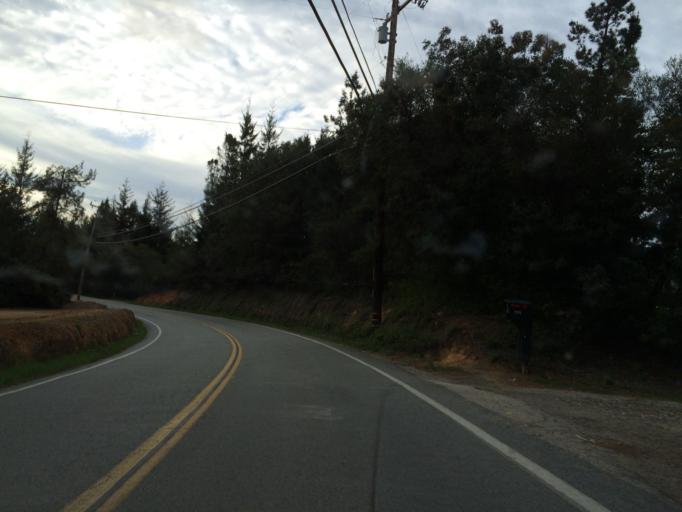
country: US
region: California
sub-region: Santa Cruz County
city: Bonny Doon
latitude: 37.0642
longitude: -122.1231
